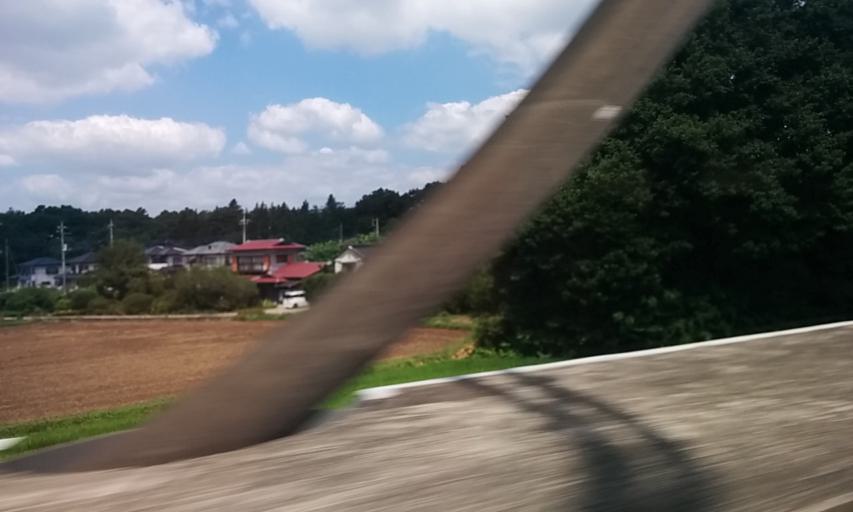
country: JP
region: Tochigi
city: Yaita
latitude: 36.7873
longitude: 139.9535
